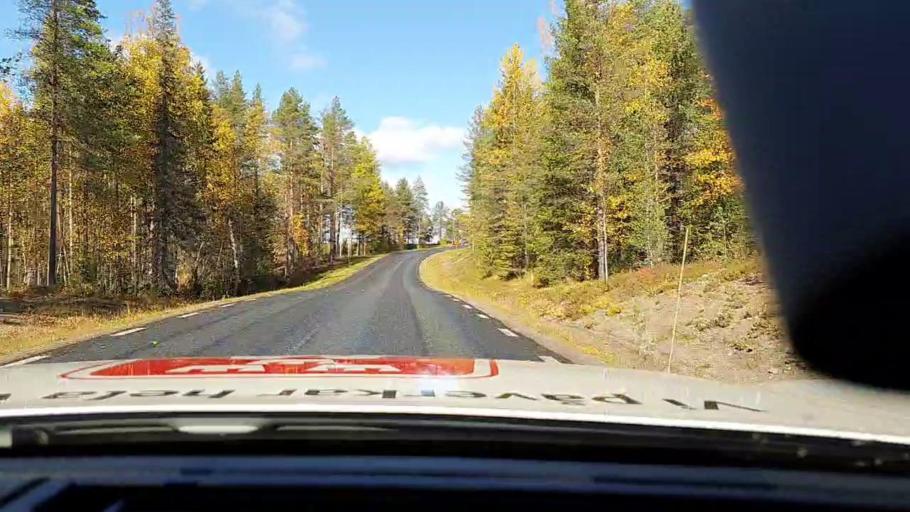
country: SE
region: Vaesterbotten
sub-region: Skelleftea Kommun
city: Langsele
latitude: 65.0024
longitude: 20.0914
